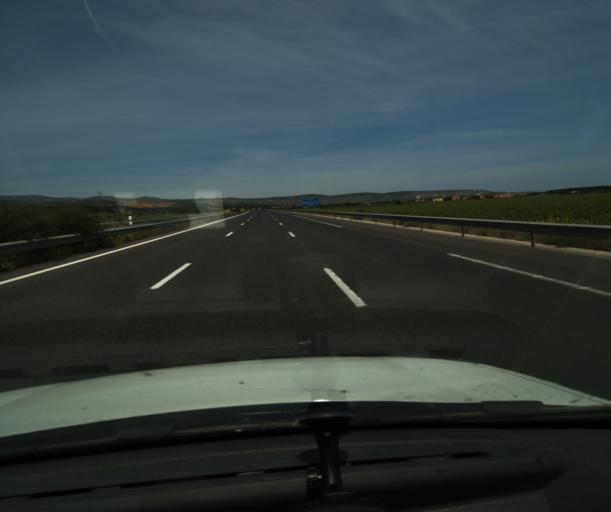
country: FR
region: Languedoc-Roussillon
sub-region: Departement des Pyrenees-Orientales
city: Salses-le-Chateau
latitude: 42.8181
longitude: 2.9083
